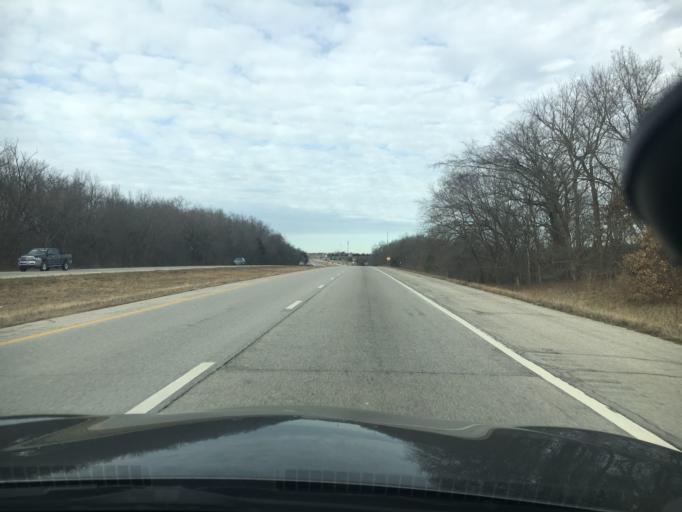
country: US
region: Missouri
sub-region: Cass County
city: Belton
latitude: 38.8179
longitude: -94.6759
